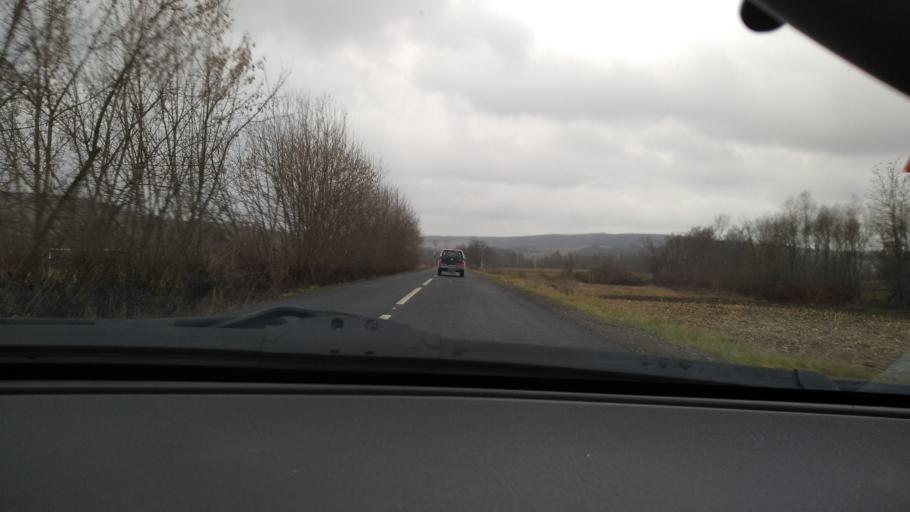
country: RO
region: Mures
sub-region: Comuna Magherani
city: Magherani
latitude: 46.5585
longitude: 24.8927
